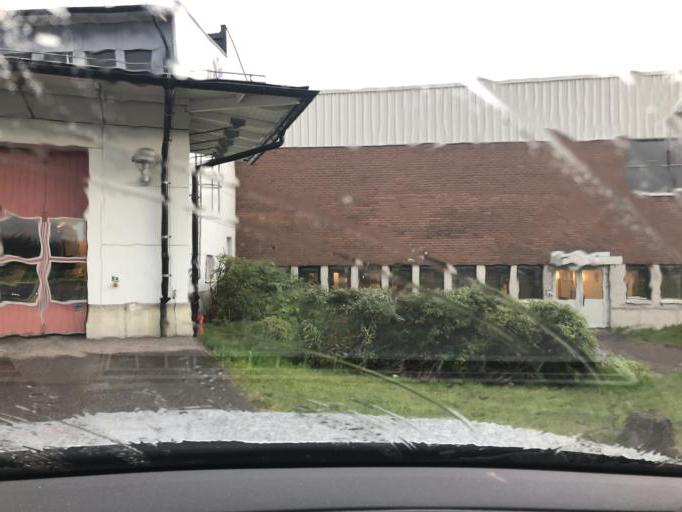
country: SE
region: Vaesternorrland
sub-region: Sundsvalls Kommun
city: Sundsvall
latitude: 62.4070
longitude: 17.3029
